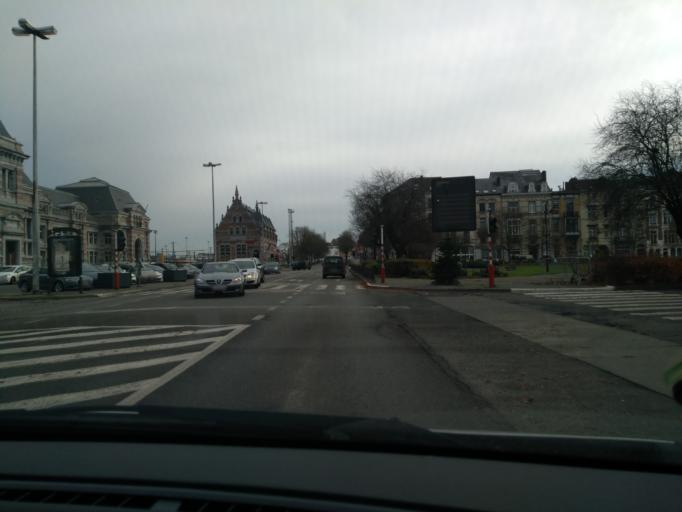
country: BE
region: Wallonia
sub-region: Province du Hainaut
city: Tournai
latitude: 50.6126
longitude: 3.3958
